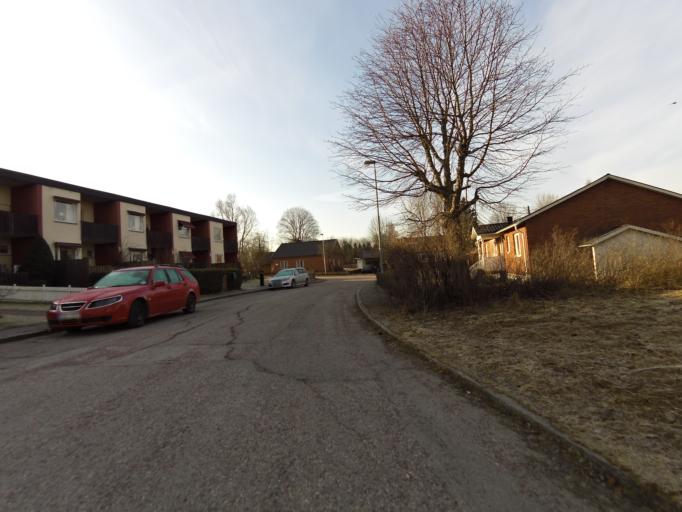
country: SE
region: Gaevleborg
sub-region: Gavle Kommun
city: Gavle
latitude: 60.6569
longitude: 17.1280
